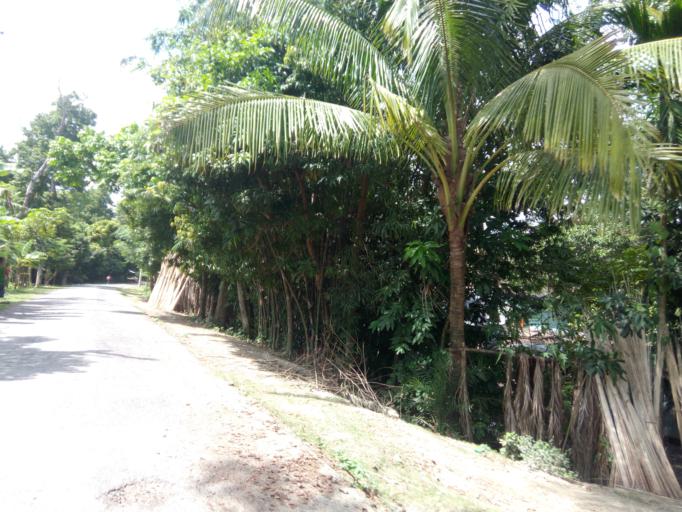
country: BD
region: Khulna
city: Kalia
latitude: 23.0154
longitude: 89.7188
